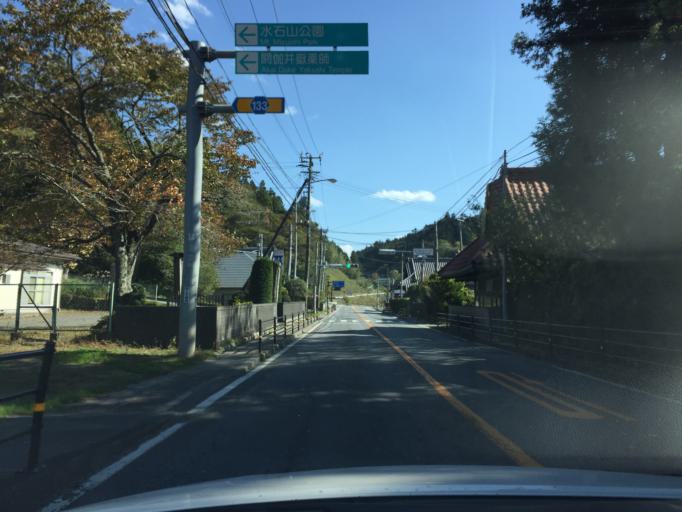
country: JP
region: Fukushima
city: Iwaki
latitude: 37.0985
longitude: 140.7772
